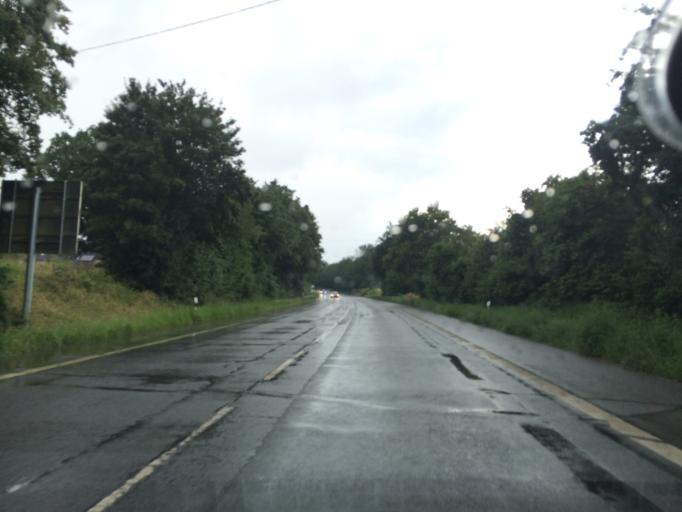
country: DE
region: North Rhine-Westphalia
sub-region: Regierungsbezirk Munster
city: Haltern
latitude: 51.7789
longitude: 7.2246
